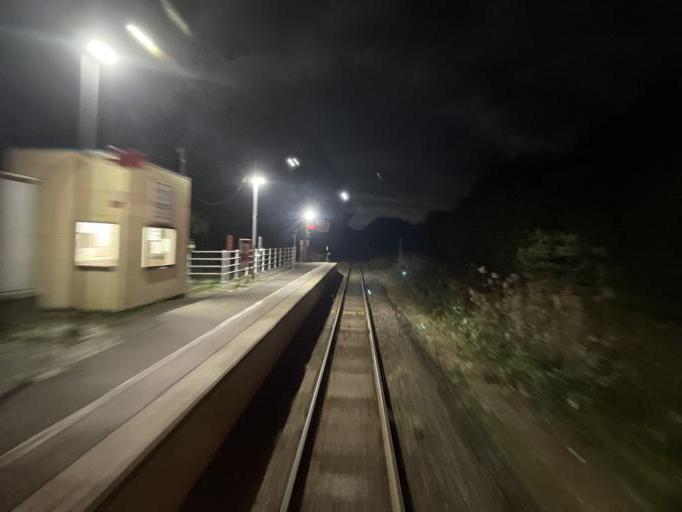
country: JP
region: Aomori
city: Mutsu
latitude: 41.2289
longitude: 141.2484
